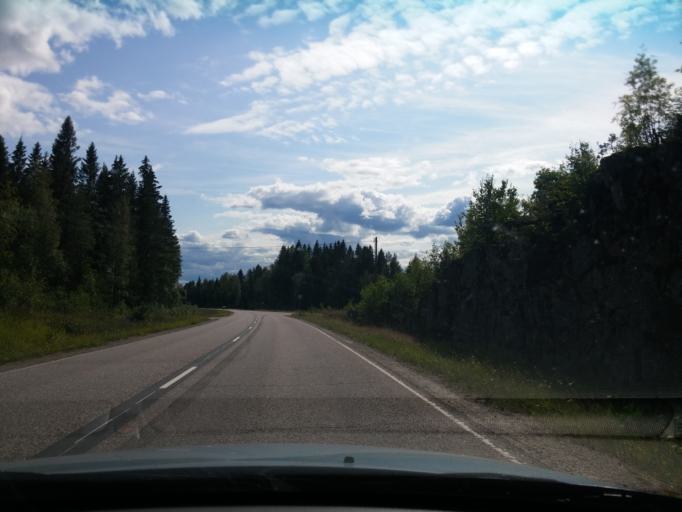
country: FI
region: Central Finland
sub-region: Keuruu
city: Keuruu
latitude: 62.2802
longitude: 24.6908
